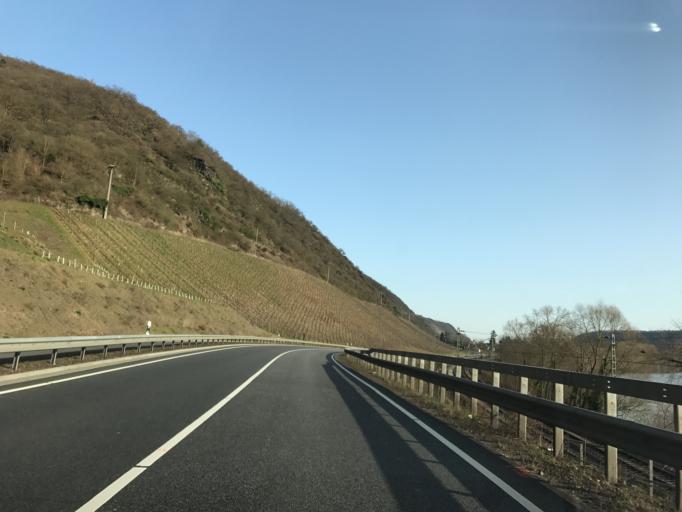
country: DE
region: Rheinland-Pfalz
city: Hammerstein
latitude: 50.4694
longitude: 7.3575
